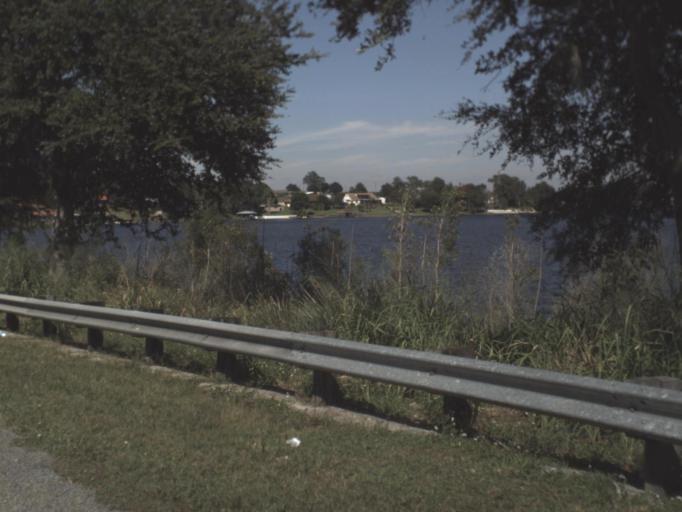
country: US
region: Florida
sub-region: Highlands County
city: Lake Placid
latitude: 27.2823
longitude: -81.3559
